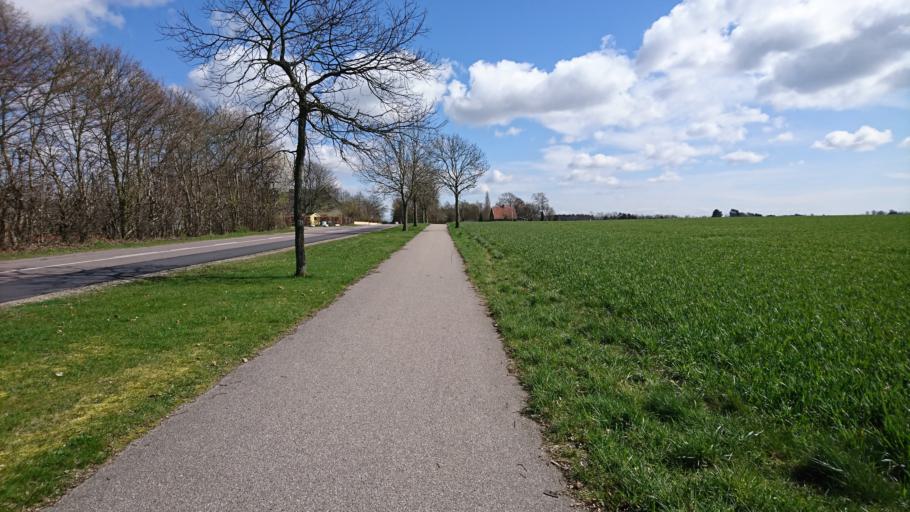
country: DK
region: Capital Region
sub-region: Egedal Kommune
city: Vekso
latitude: 55.7707
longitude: 12.2258
